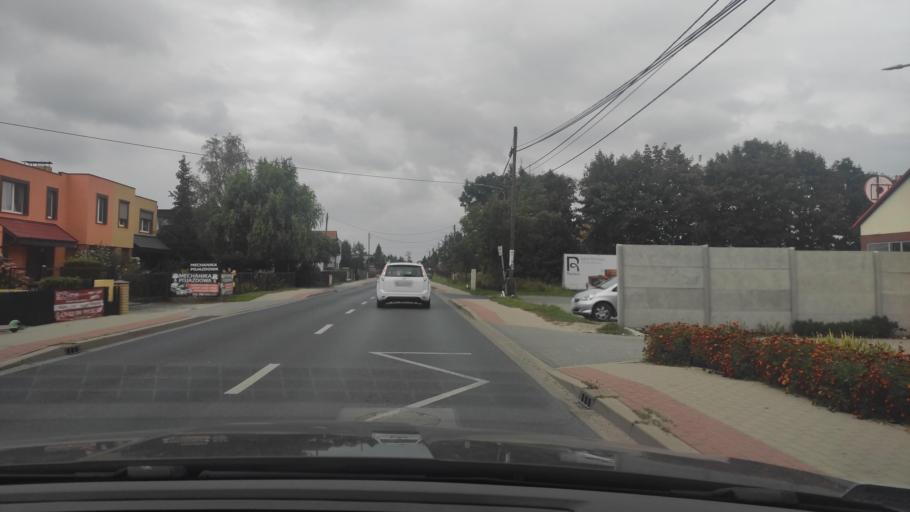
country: PL
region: Greater Poland Voivodeship
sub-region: Powiat poznanski
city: Swarzedz
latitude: 52.3906
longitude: 17.0757
